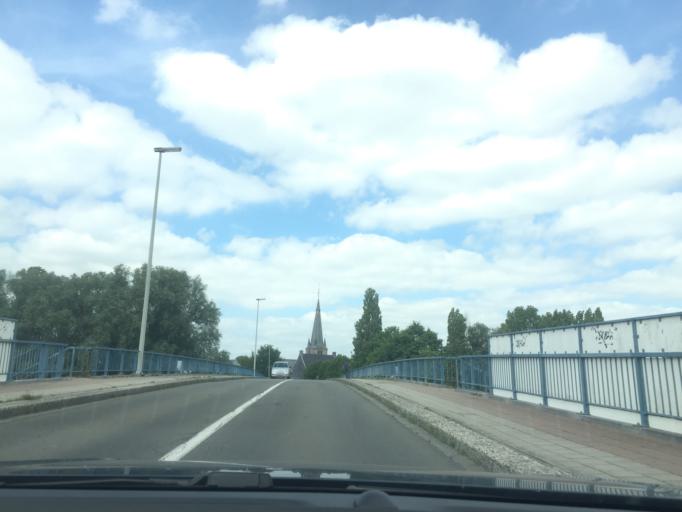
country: BE
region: Flanders
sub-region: Provincie West-Vlaanderen
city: Izegem
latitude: 50.9203
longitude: 3.2300
